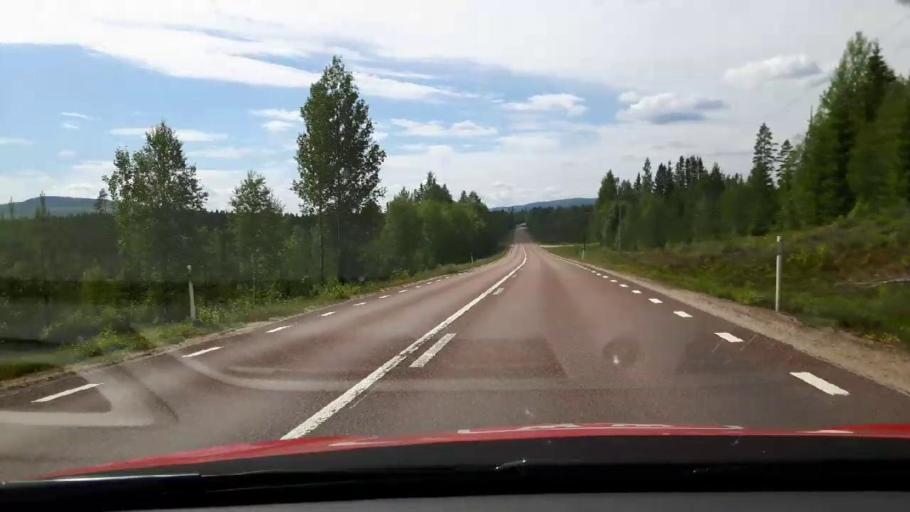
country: SE
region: Jaemtland
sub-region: Harjedalens Kommun
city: Sveg
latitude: 62.0604
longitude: 14.9122
